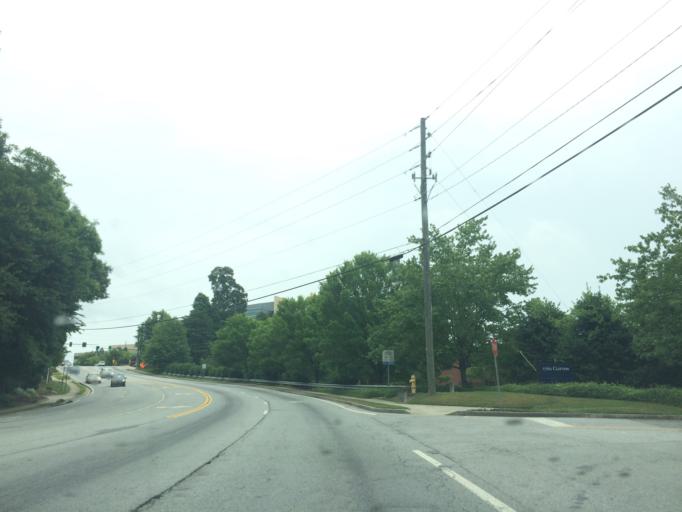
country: US
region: Georgia
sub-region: DeKalb County
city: Druid Hills
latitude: 33.8014
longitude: -84.3313
